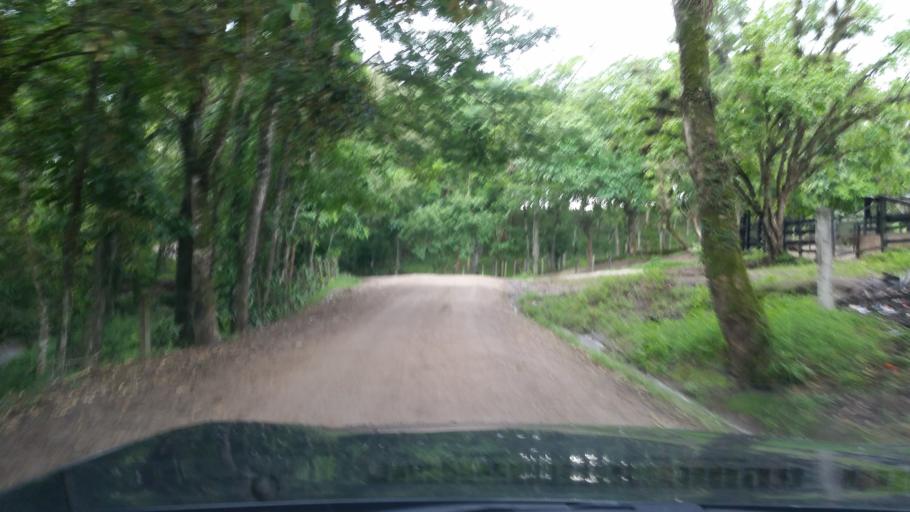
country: NI
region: Matagalpa
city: San Ramon
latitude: 13.0626
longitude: -85.7500
